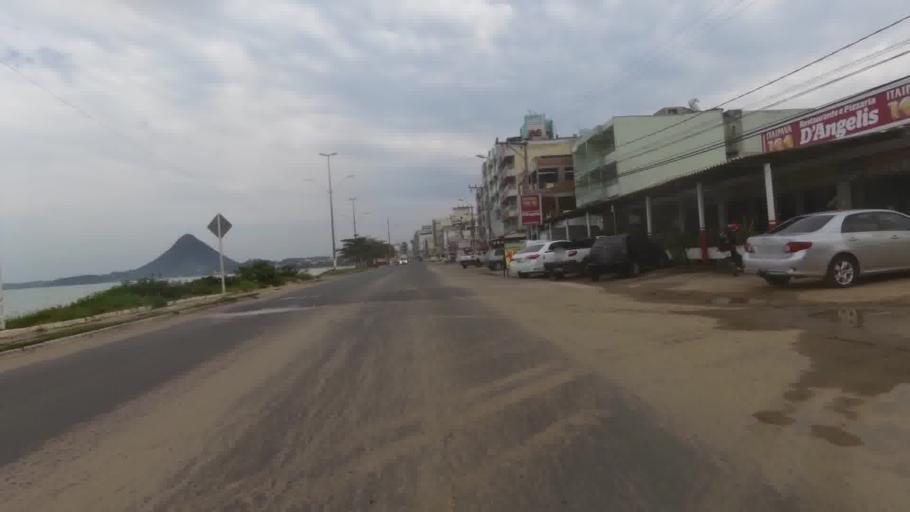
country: BR
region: Espirito Santo
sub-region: Piuma
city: Piuma
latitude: -20.8436
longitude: -40.7336
